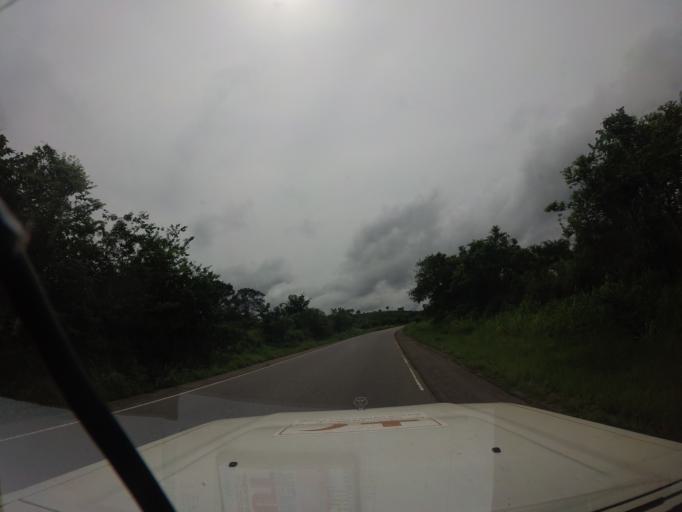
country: SL
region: Northern Province
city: Magburaka
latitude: 8.7379
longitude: -11.9595
